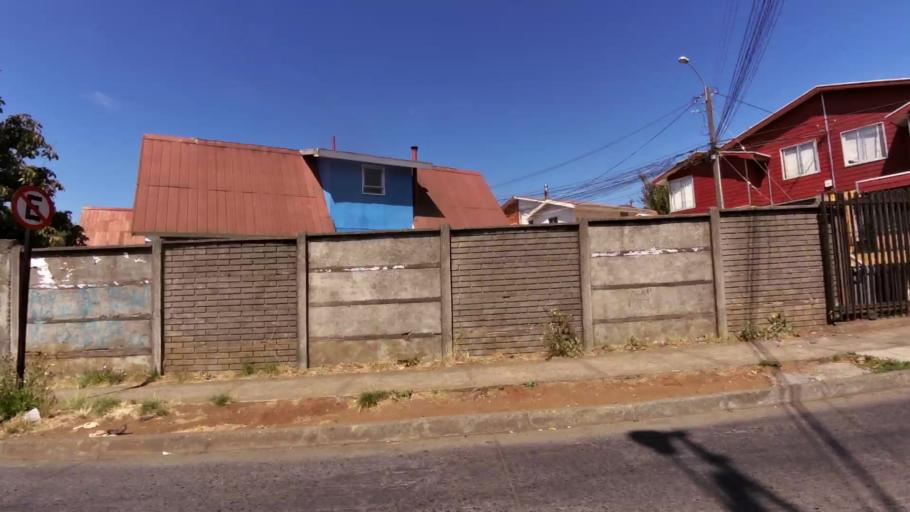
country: CL
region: Biobio
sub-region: Provincia de Concepcion
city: Concepcion
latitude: -36.7830
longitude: -73.0423
